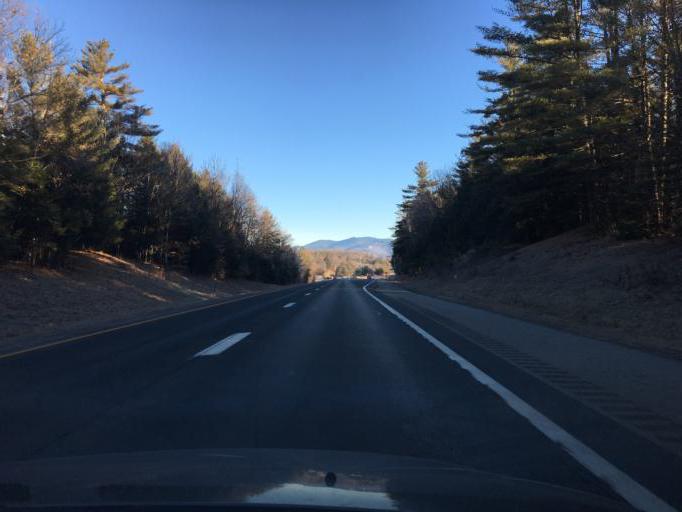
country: US
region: New Hampshire
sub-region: Grafton County
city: Plymouth
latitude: 43.8059
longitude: -71.6741
